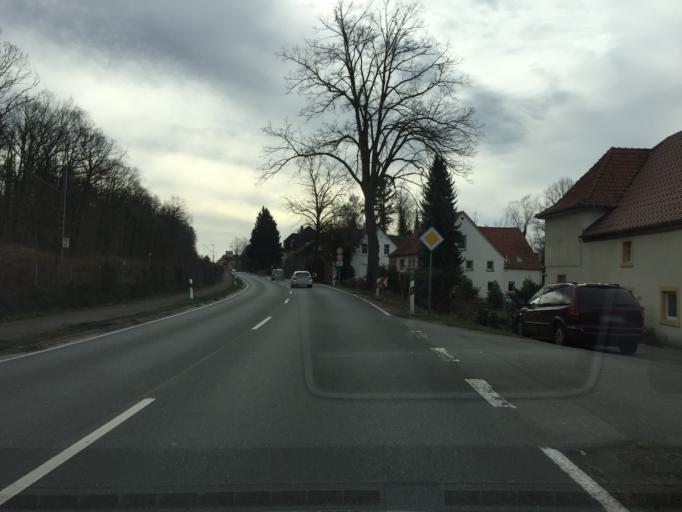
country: DE
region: North Rhine-Westphalia
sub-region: Regierungsbezirk Detmold
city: Lage
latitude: 52.0050
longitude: 8.7742
